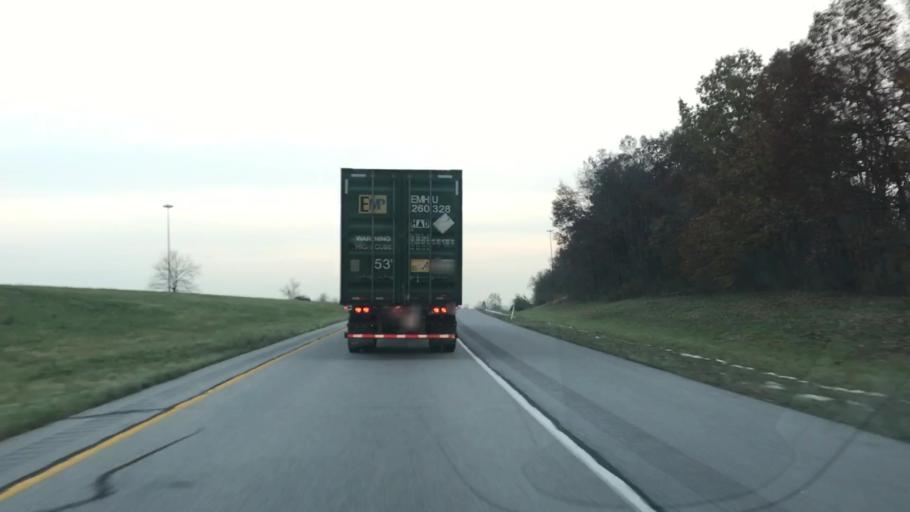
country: US
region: Pennsylvania
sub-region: Dauphin County
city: Harrisburg
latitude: 40.3019
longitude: -76.8820
